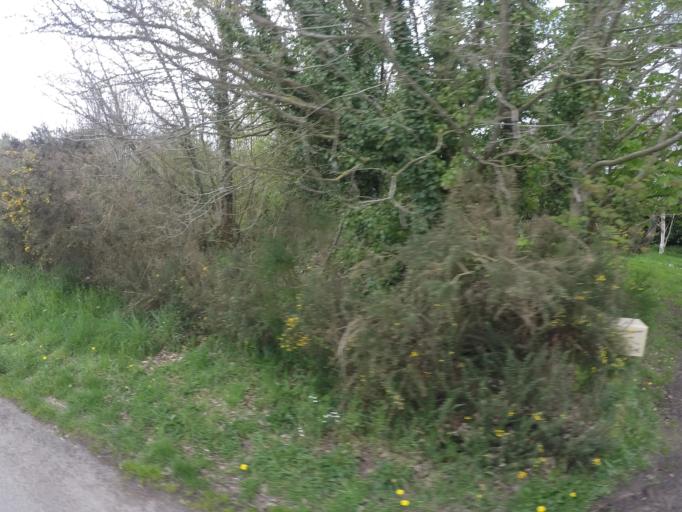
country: FR
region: Brittany
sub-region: Departement des Cotes-d'Armor
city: Plouha
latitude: 48.7006
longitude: -2.9358
